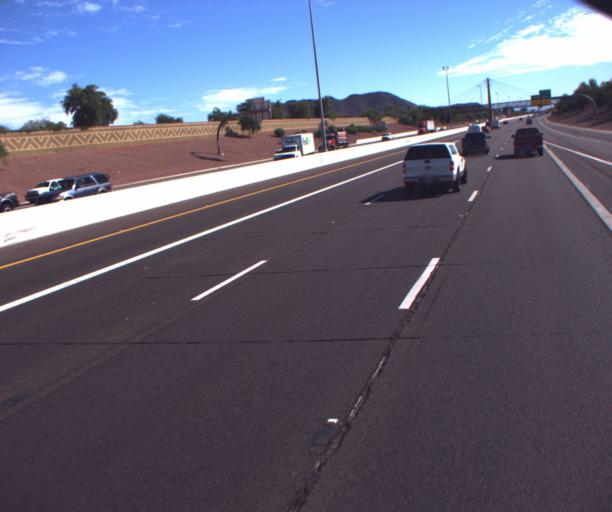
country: US
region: Arizona
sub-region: Maricopa County
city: Peoria
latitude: 33.6680
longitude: -112.1982
